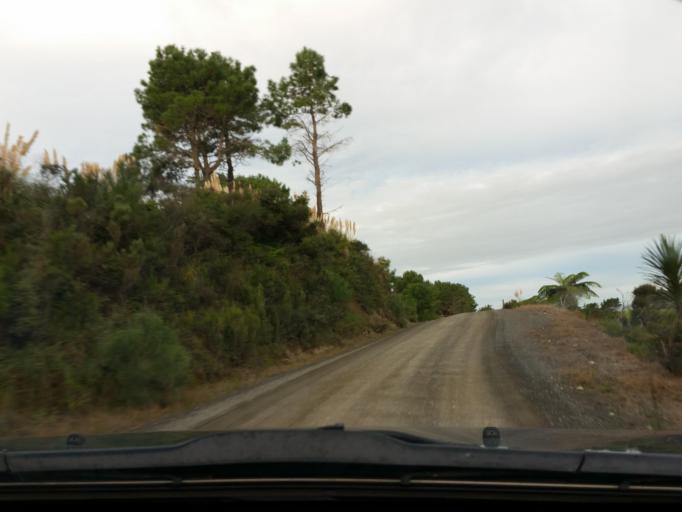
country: NZ
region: Northland
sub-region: Kaipara District
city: Dargaville
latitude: -35.9106
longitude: 173.7691
